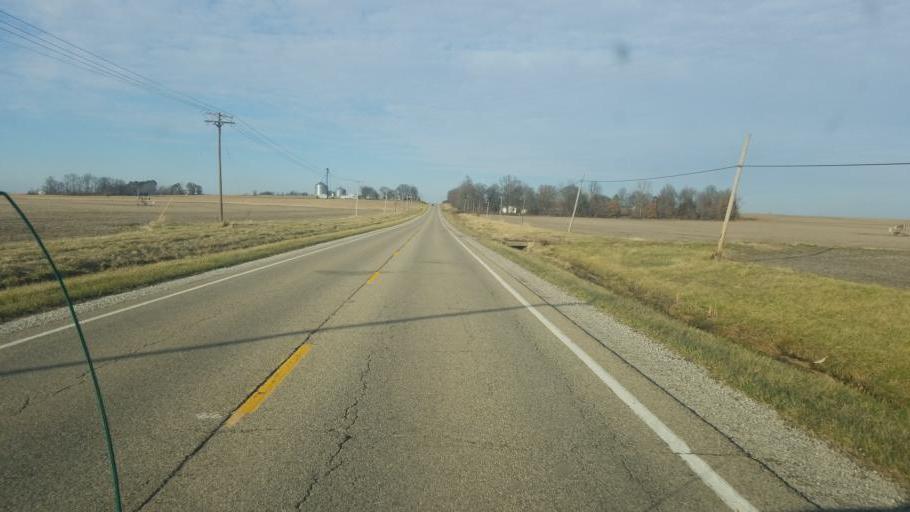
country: US
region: Illinois
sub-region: Lawrence County
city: Lawrenceville
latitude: 38.6502
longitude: -87.6943
